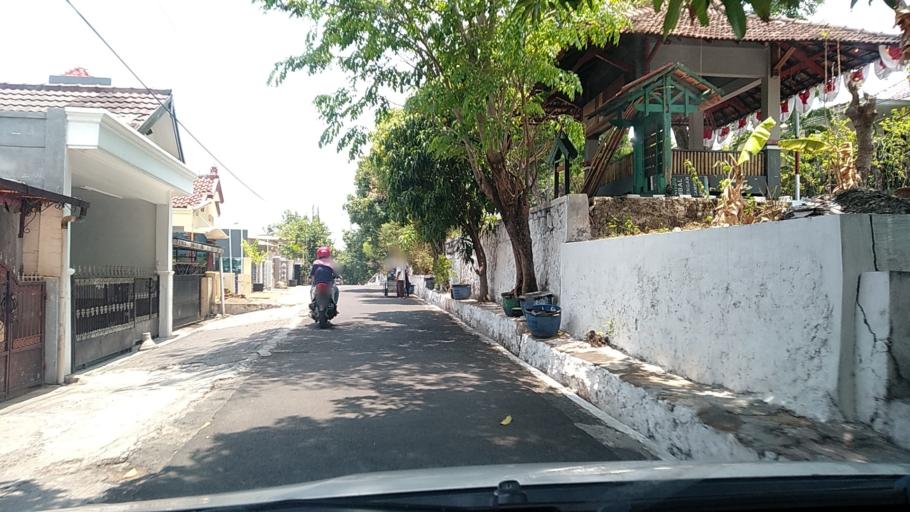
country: ID
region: Central Java
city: Mranggen
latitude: -7.0308
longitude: 110.4719
